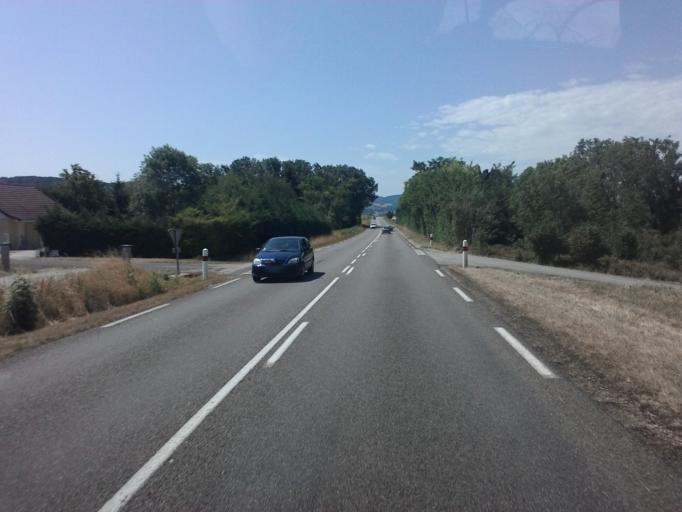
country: FR
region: Franche-Comte
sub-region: Departement du Jura
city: Montmorot
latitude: 46.6324
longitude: 5.4921
